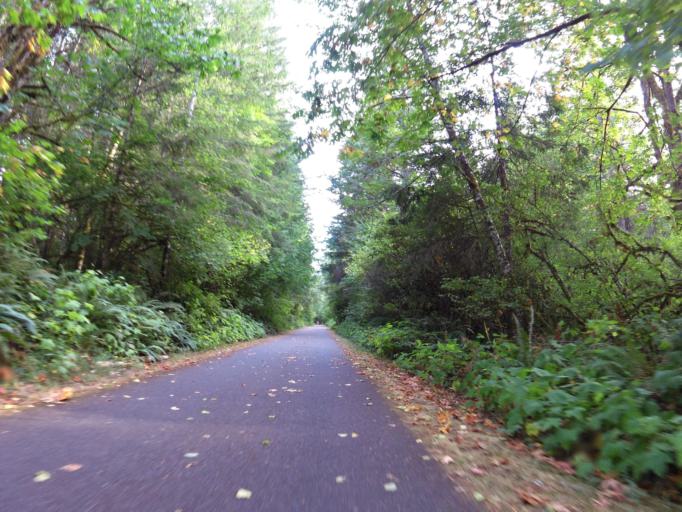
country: US
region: Washington
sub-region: Thurston County
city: Lacey
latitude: 46.9733
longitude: -122.8128
